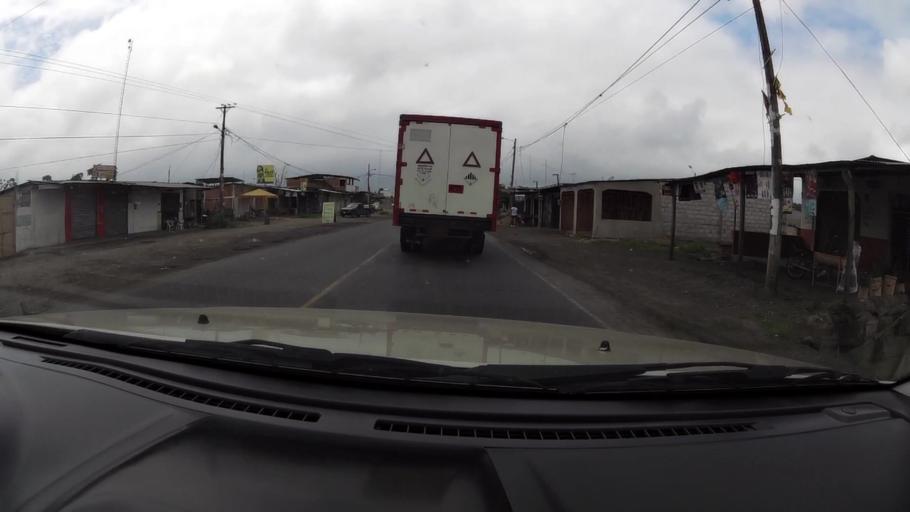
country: EC
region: Guayas
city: Balao
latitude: -2.9036
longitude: -79.7064
